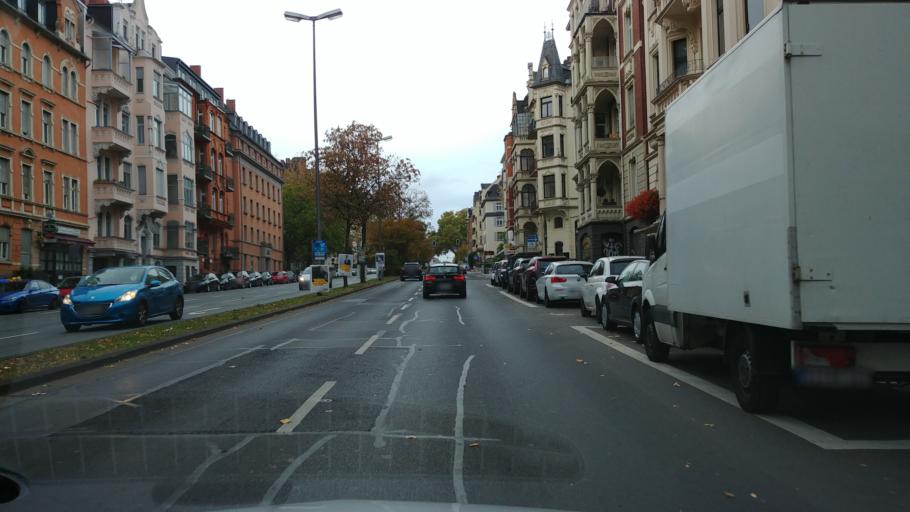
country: DE
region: Hesse
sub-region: Regierungsbezirk Darmstadt
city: Wiesbaden
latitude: 50.0741
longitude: 8.2311
